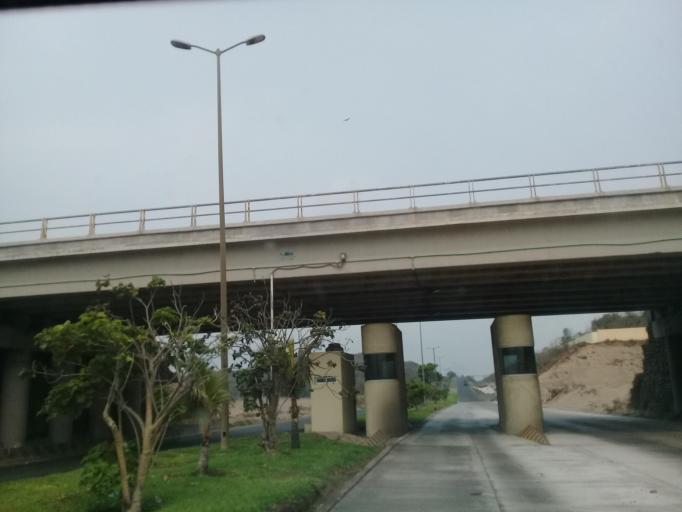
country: MX
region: Veracruz
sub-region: Veracruz
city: Colonia el Renacimiento
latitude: 19.2275
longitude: -96.1999
